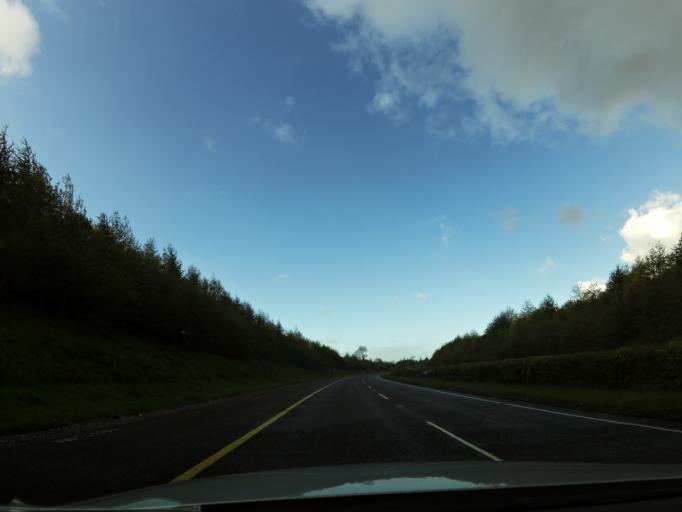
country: IE
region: Munster
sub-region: County Limerick
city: Annacotty
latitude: 52.6627
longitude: -8.5199
